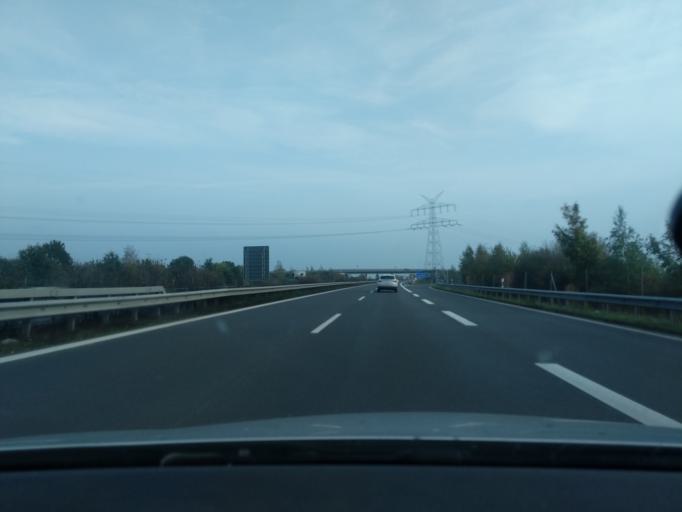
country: DE
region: Lower Saxony
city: Agathenburg
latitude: 53.5804
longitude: 9.5135
